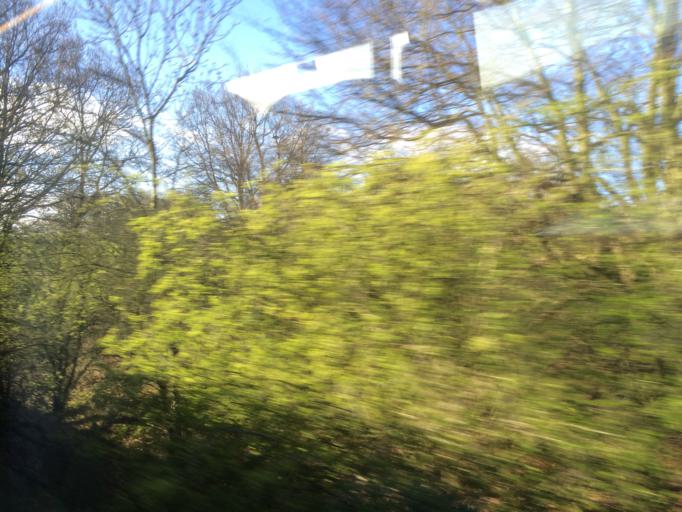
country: GB
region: Scotland
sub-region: Stirling
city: Bannockburn
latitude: 56.0893
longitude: -3.8941
